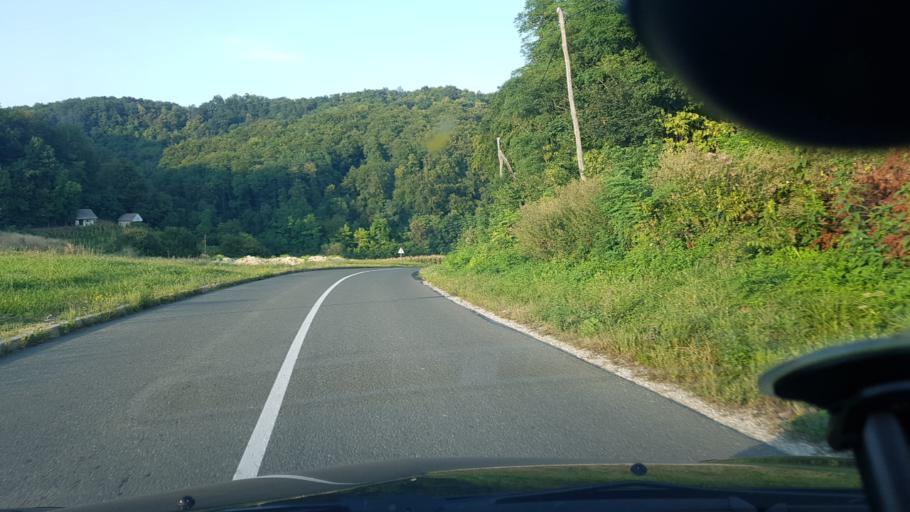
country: HR
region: Krapinsko-Zagorska
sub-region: Grad Krapina
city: Krapina
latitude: 46.1682
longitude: 15.8450
